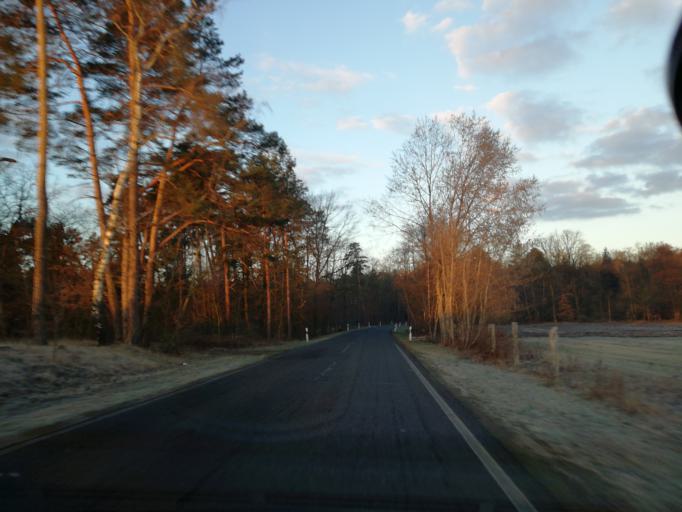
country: DE
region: Brandenburg
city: Calau
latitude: 51.7260
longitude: 13.8978
